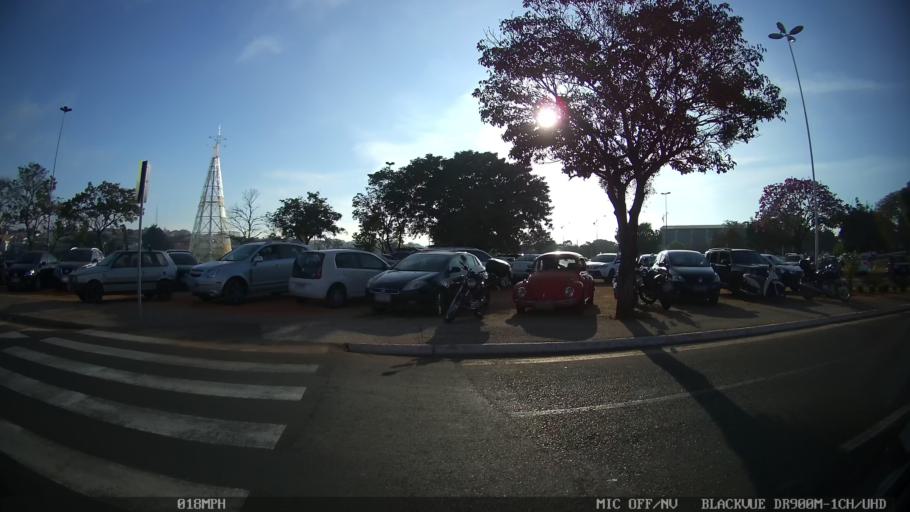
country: BR
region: Sao Paulo
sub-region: Sao Jose Do Rio Preto
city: Sao Jose do Rio Preto
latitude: -20.8105
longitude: -49.3681
